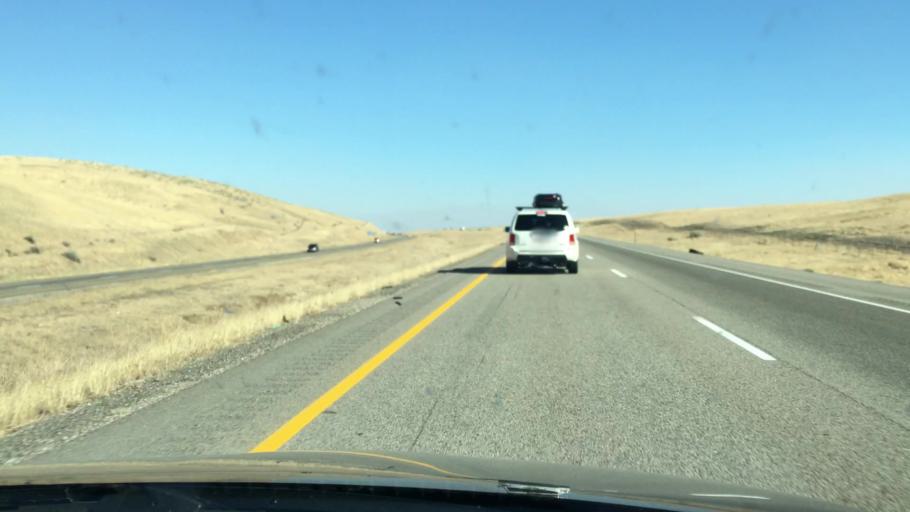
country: US
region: Idaho
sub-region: Ada County
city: Boise
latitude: 43.4927
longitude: -116.1279
